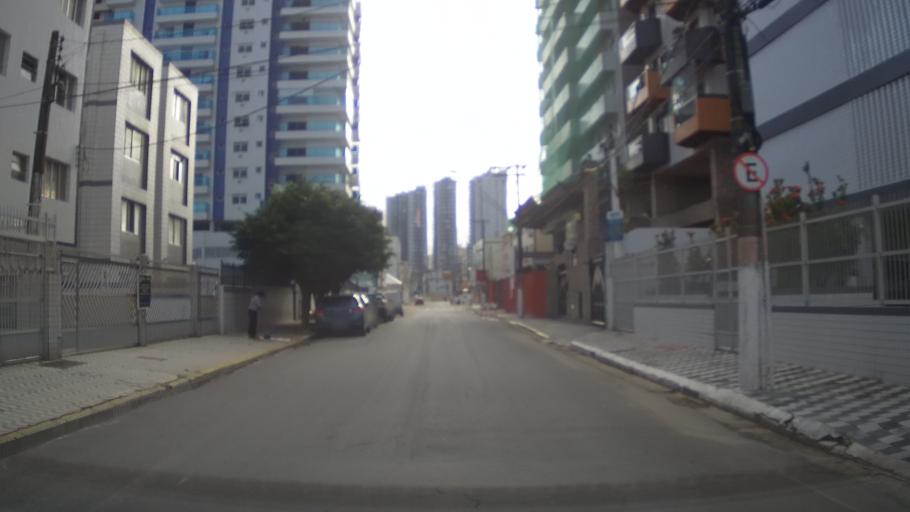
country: BR
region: Sao Paulo
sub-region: Praia Grande
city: Praia Grande
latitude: -24.0124
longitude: -46.4107
